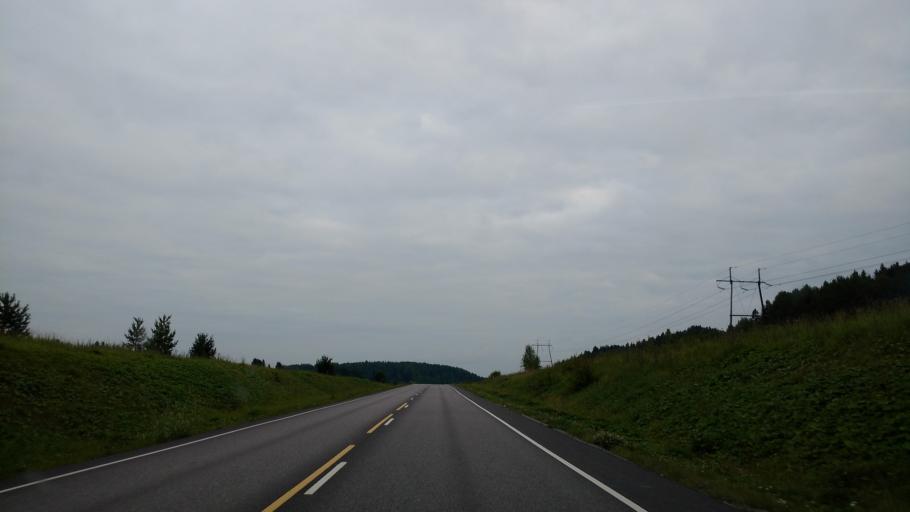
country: FI
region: Varsinais-Suomi
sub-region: Salo
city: Halikko
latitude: 60.3958
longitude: 23.0542
